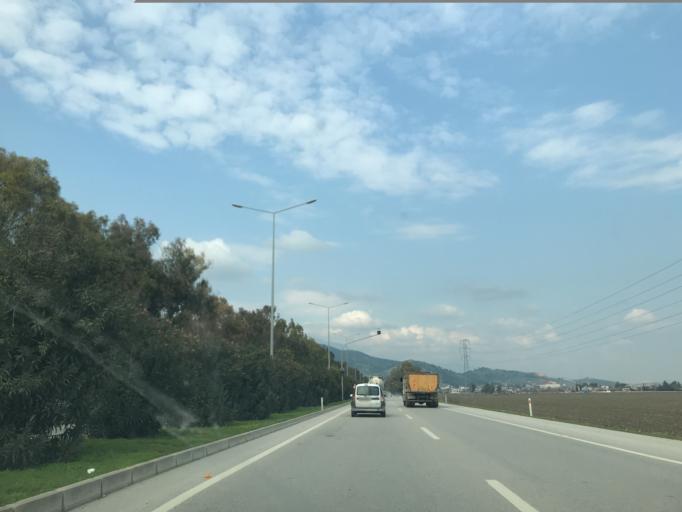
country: TR
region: Hatay
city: Serinyol
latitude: 36.3756
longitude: 36.2272
